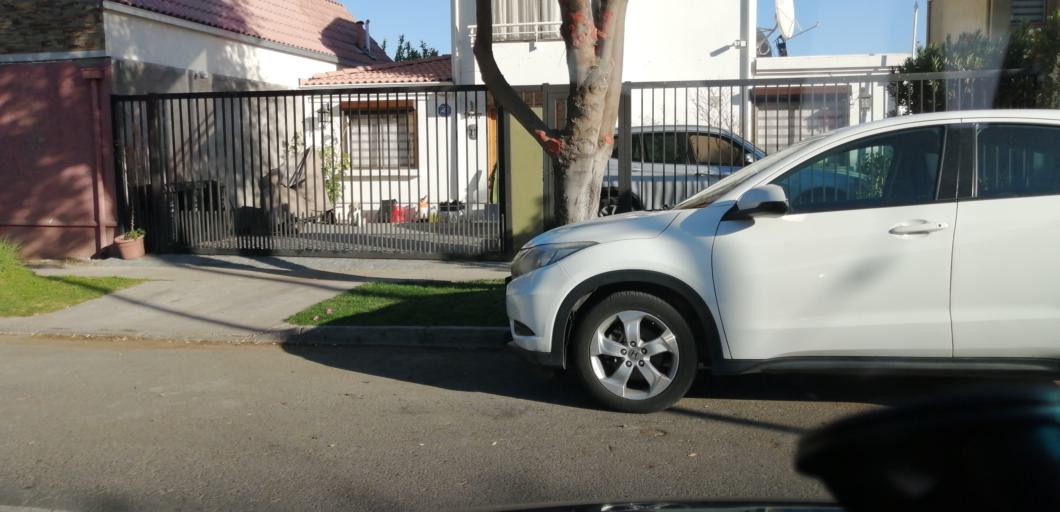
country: CL
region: Santiago Metropolitan
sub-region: Provincia de Santiago
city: Lo Prado
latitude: -33.4475
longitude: -70.8383
